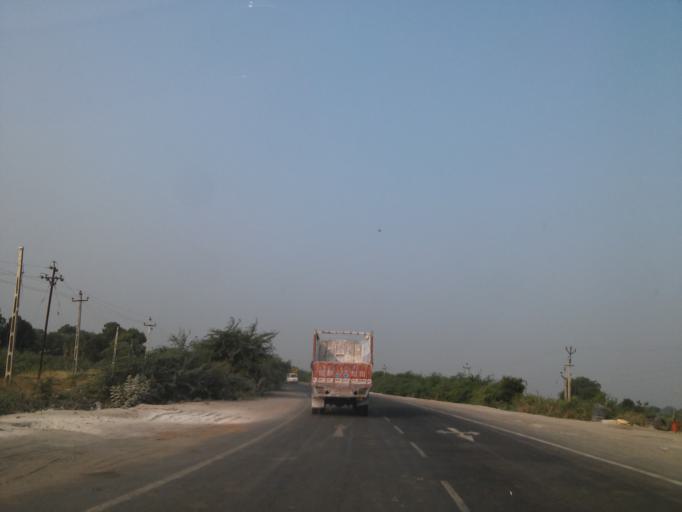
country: IN
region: Gujarat
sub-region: Kachchh
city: Anjar
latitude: 23.3124
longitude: 70.1207
